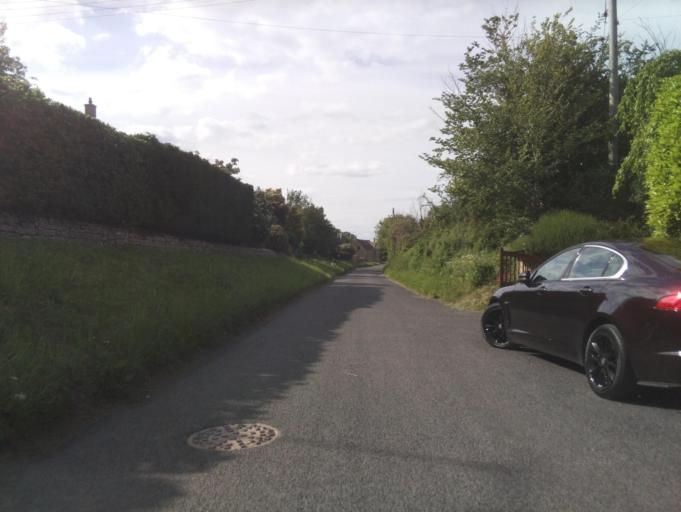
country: GB
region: England
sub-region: Gloucestershire
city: Chipping Campden
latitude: 52.0642
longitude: -1.8142
